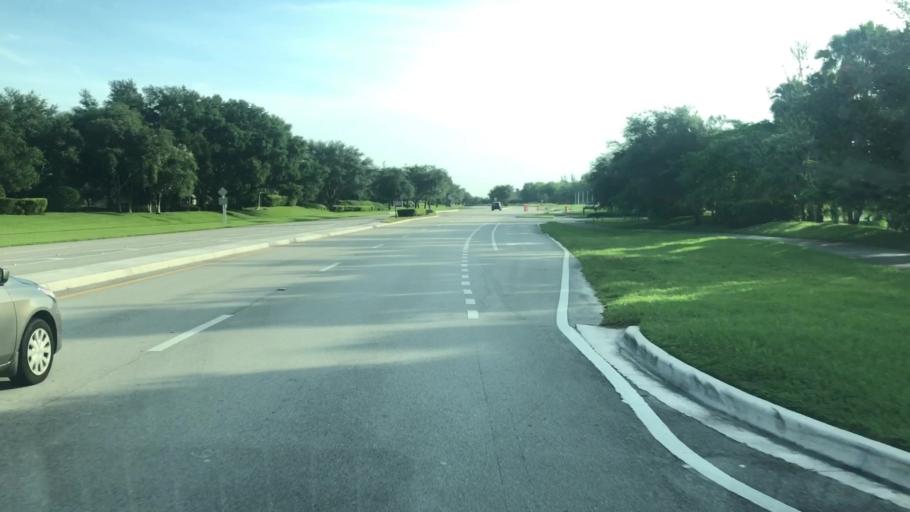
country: US
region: Florida
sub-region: Broward County
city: Parkland
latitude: 26.3127
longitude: -80.2528
